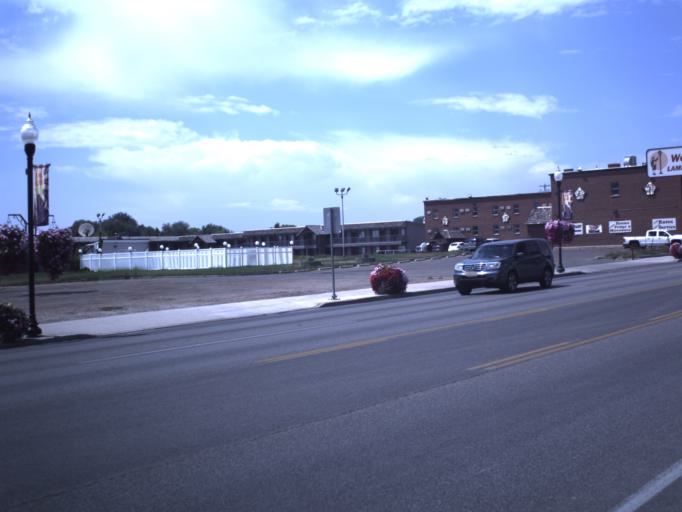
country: US
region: Utah
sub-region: Uintah County
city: Vernal
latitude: 40.4558
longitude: -109.5249
